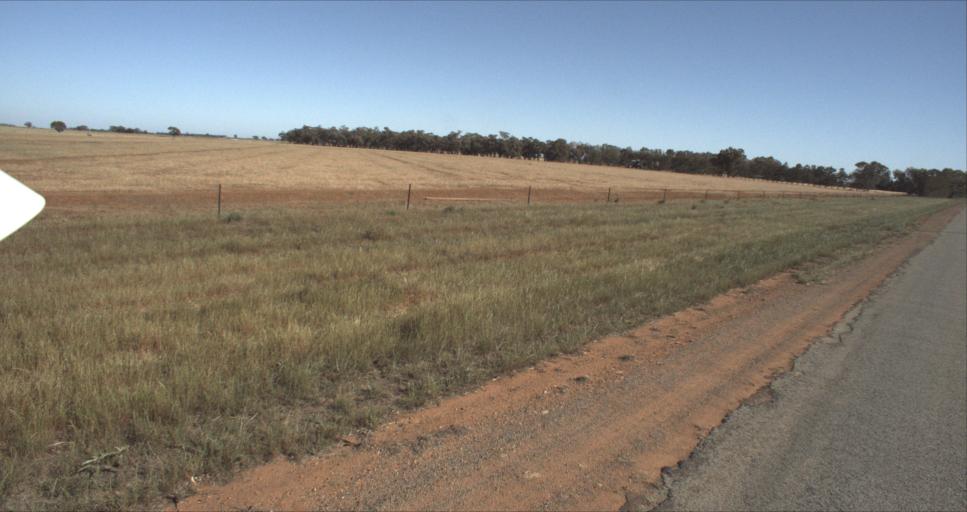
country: AU
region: New South Wales
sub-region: Leeton
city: Leeton
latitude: -34.5804
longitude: 146.3089
